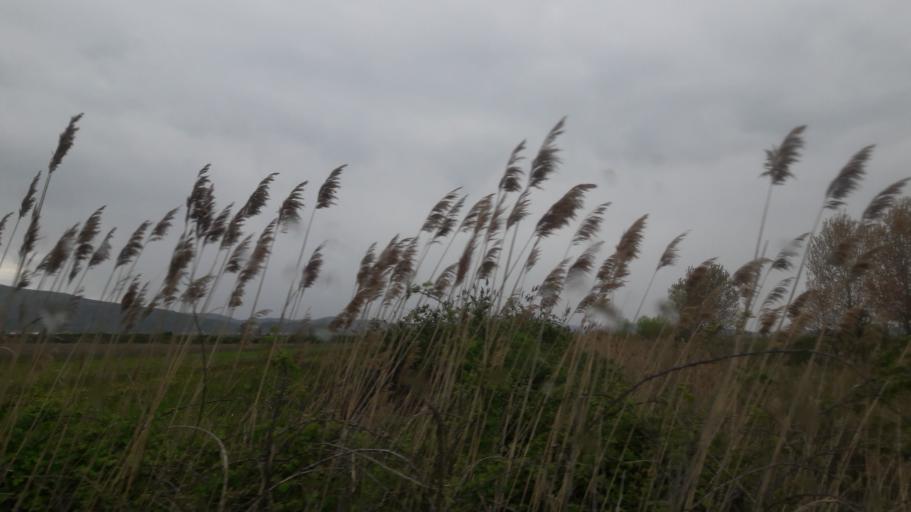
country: AL
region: Shkoder
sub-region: Rrethi i Shkodres
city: Berdica e Madhe
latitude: 41.9619
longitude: 19.5033
